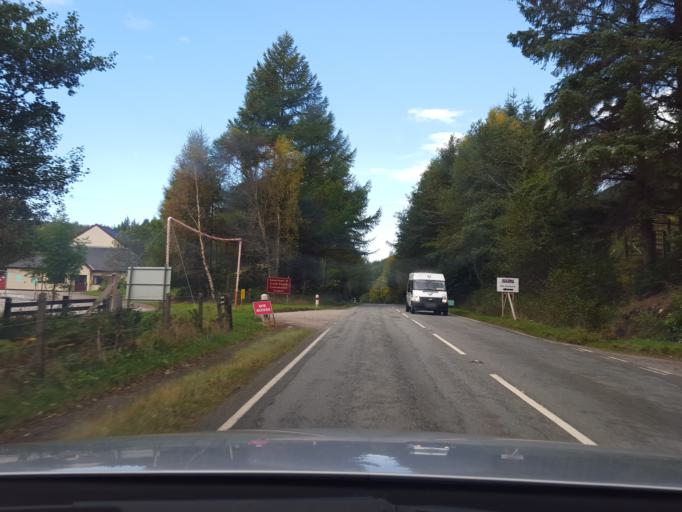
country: GB
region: Scotland
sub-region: Highland
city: Fort William
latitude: 57.2386
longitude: -5.4426
